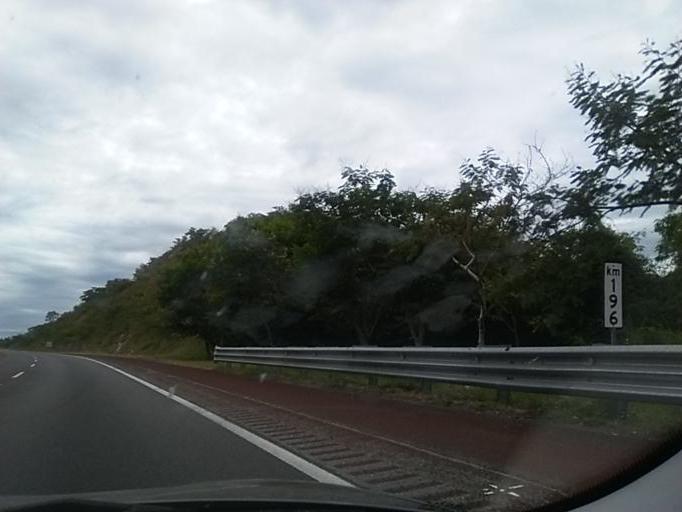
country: MX
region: Guerrero
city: Copalillo
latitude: 18.0858
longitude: -99.2287
